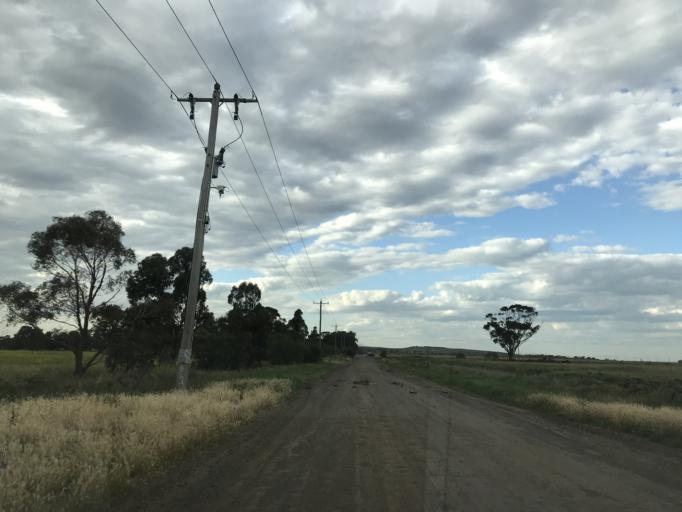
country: AU
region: Victoria
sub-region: Wyndham
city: Truganina
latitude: -37.8104
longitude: 144.7230
